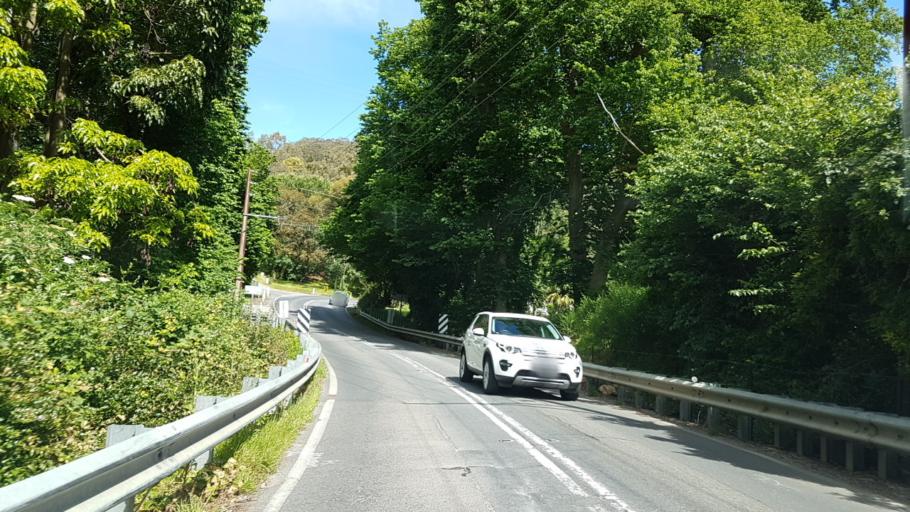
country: AU
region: South Australia
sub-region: Adelaide Hills
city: Adelaide Hills
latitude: -34.9217
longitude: 138.7178
